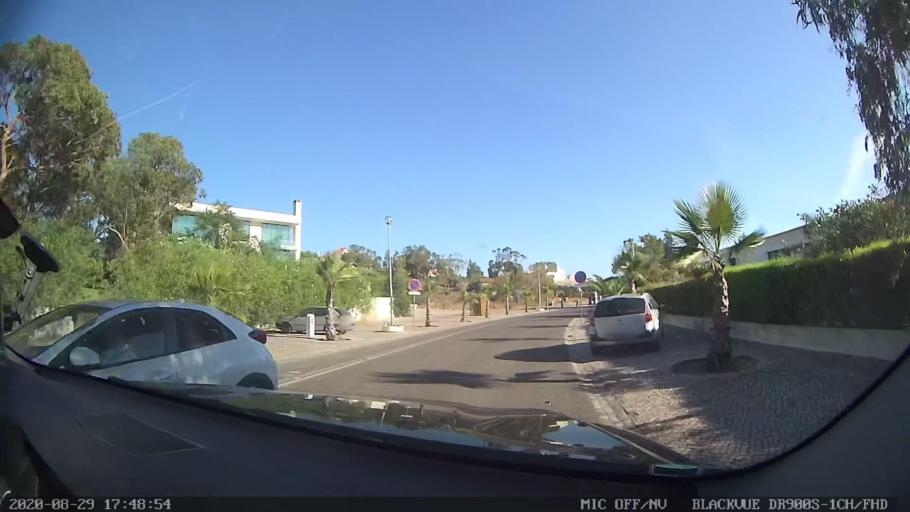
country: PT
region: Setubal
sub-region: Setubal
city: Setubal
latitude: 38.4552
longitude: -8.8577
